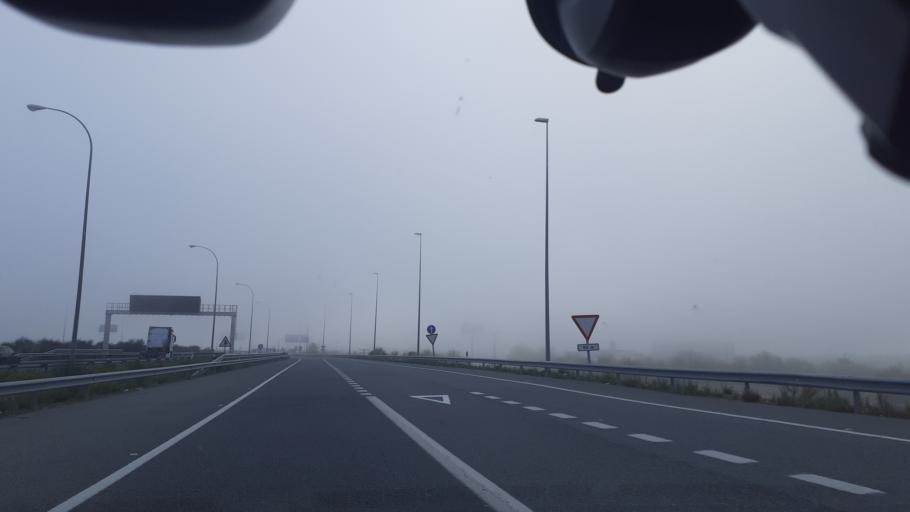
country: ES
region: Madrid
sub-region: Provincia de Madrid
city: Vicalvaro
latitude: 40.3979
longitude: -3.5763
